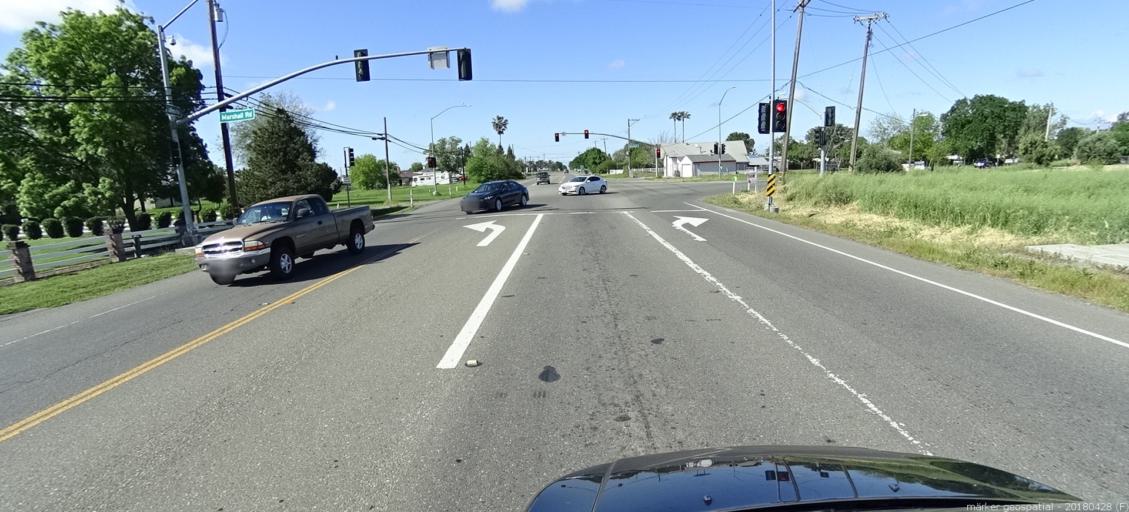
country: US
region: California
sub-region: Yolo County
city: West Sacramento
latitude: 38.5353
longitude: -121.5536
